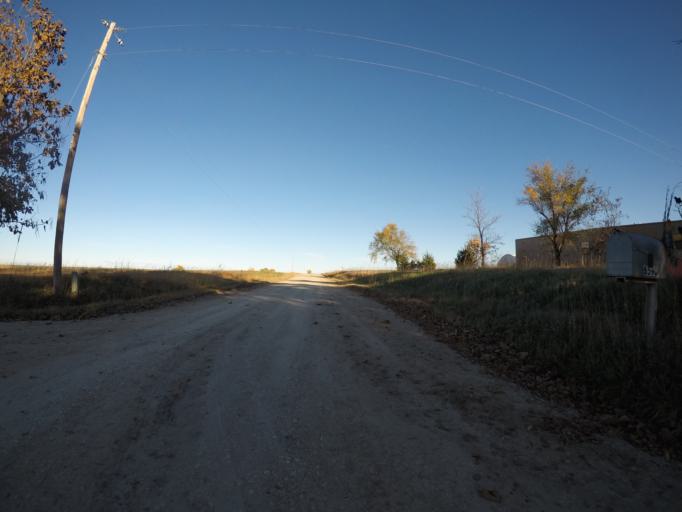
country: US
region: Kansas
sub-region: Riley County
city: Manhattan
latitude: 39.2691
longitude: -96.6958
